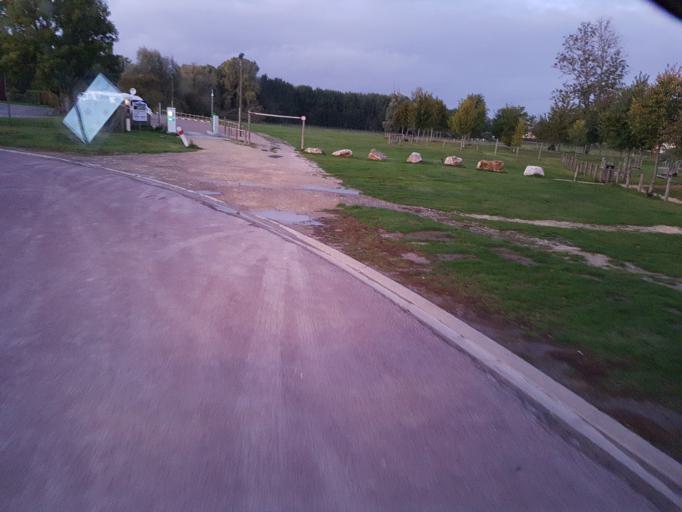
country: FR
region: Picardie
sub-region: Departement de la Somme
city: Ailly-sur-Noye
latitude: 49.7471
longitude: 2.3553
